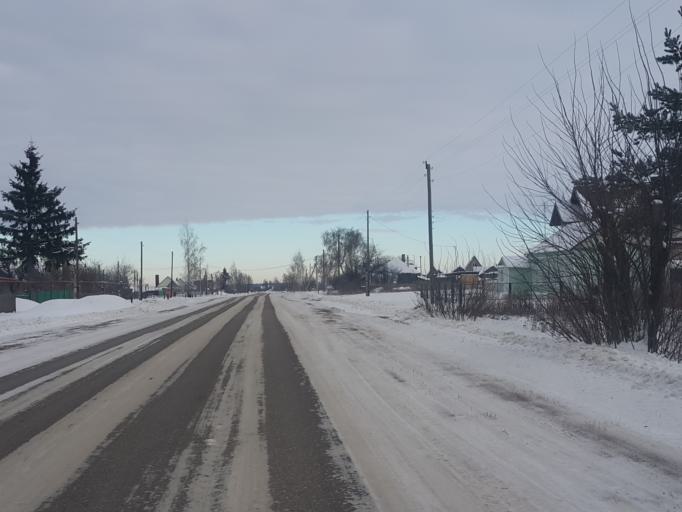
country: RU
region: Tambov
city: Platonovka
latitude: 52.8293
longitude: 41.8064
